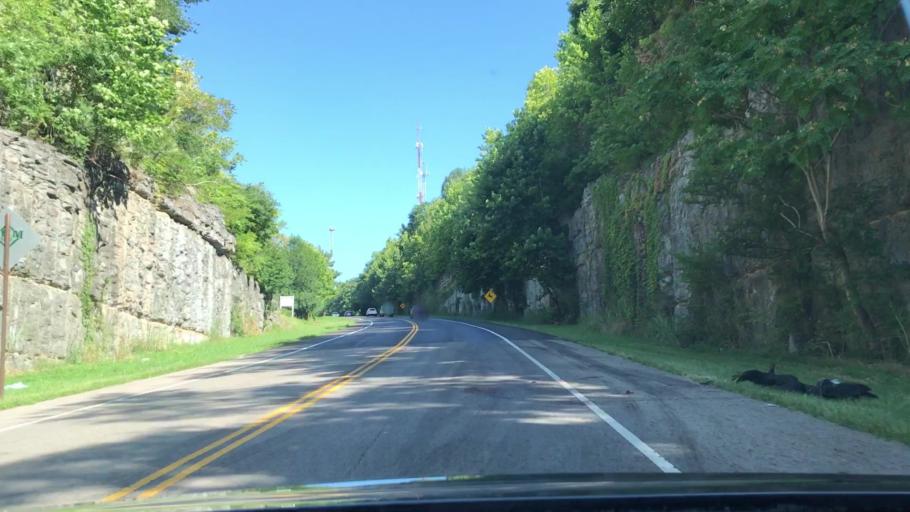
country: US
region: Tennessee
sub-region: Williamson County
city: Franklin
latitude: 35.9785
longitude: -86.8411
